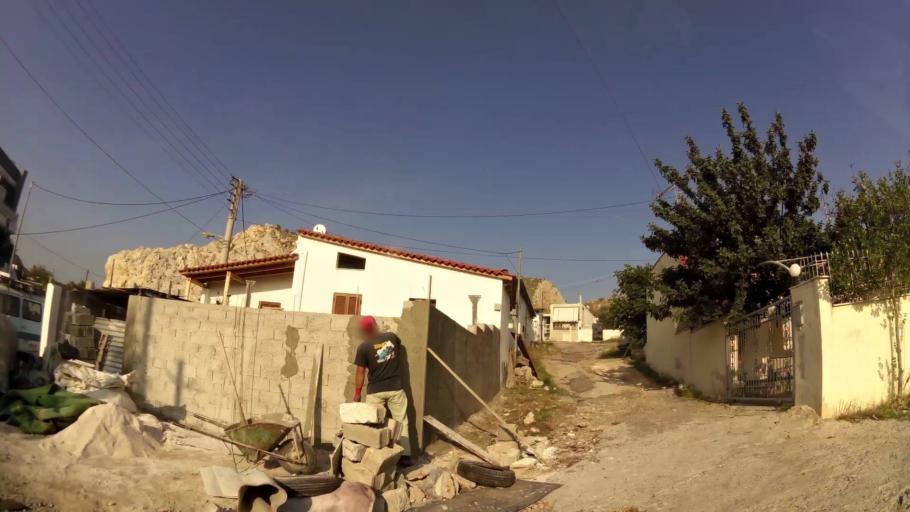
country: GR
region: Attica
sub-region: Nomos Piraios
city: Keratsini
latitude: 37.9679
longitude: 23.6327
